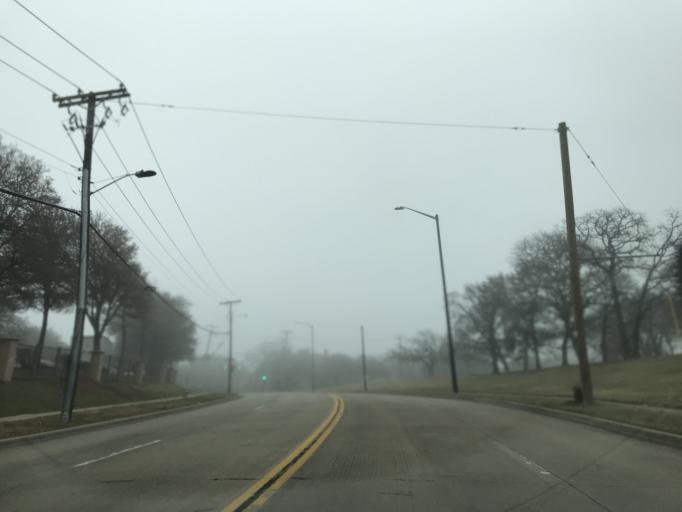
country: US
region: Texas
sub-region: Tarrant County
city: Arlington
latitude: 32.7735
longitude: -97.0865
